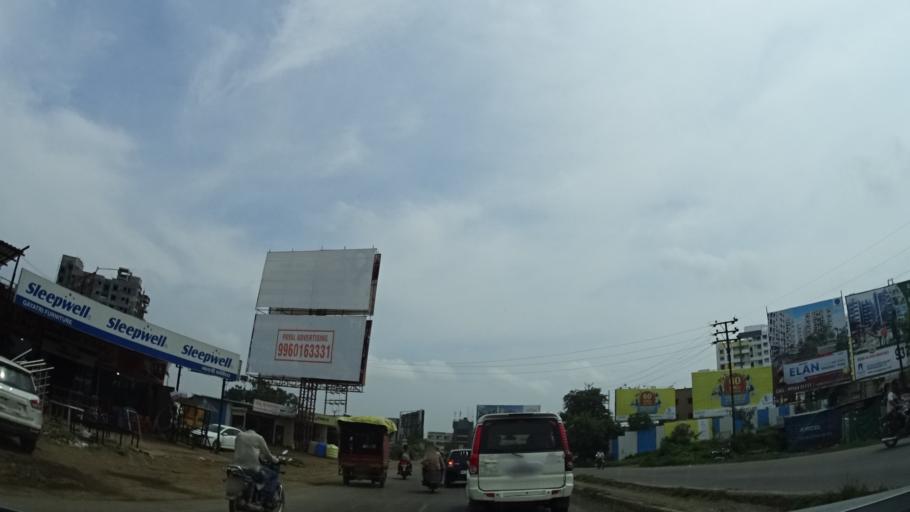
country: IN
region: Maharashtra
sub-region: Pune Division
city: Lohogaon
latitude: 18.5785
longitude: 73.9724
